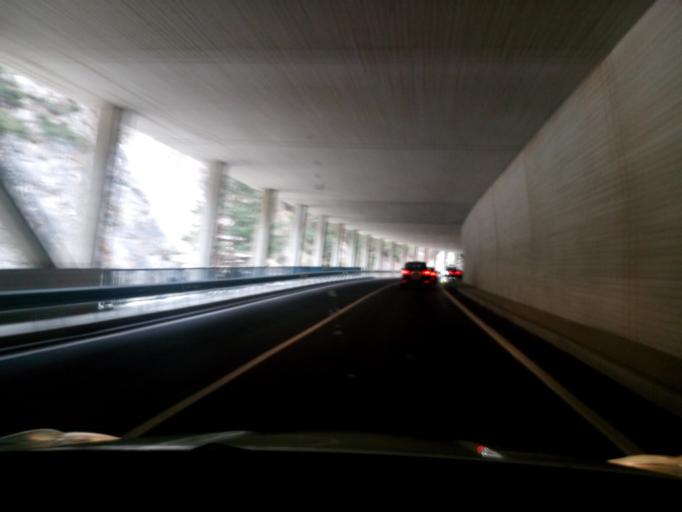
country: AT
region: Tyrol
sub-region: Politischer Bezirk Landeck
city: Nauders
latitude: 46.9129
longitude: 10.4936
